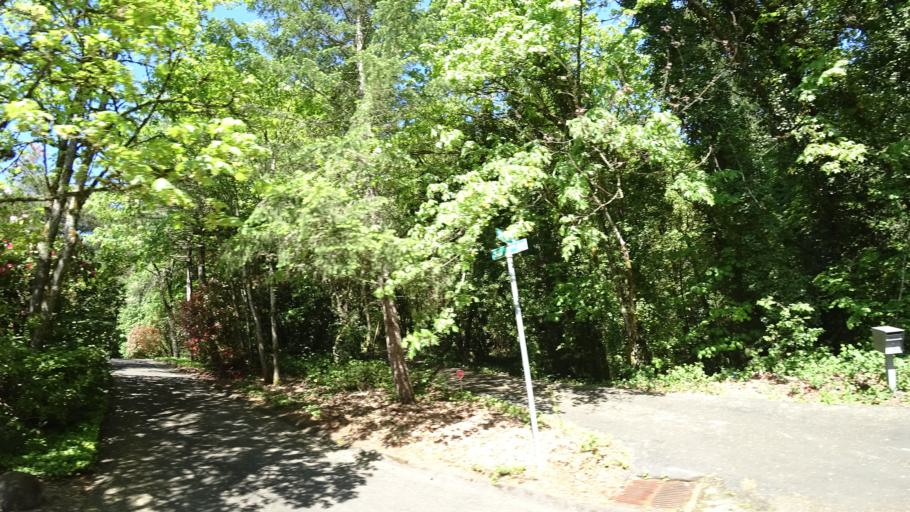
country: US
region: Oregon
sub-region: Washington County
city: West Slope
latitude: 45.4995
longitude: -122.7336
